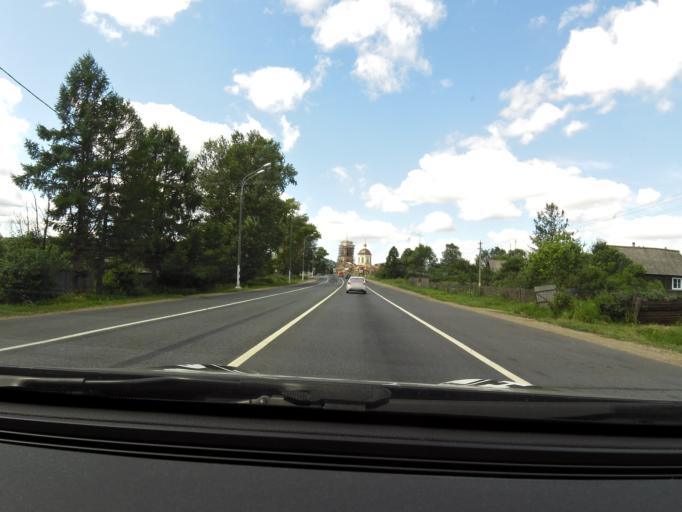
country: RU
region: Tverskaya
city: Kuzhenkino
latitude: 57.7227
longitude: 34.0888
